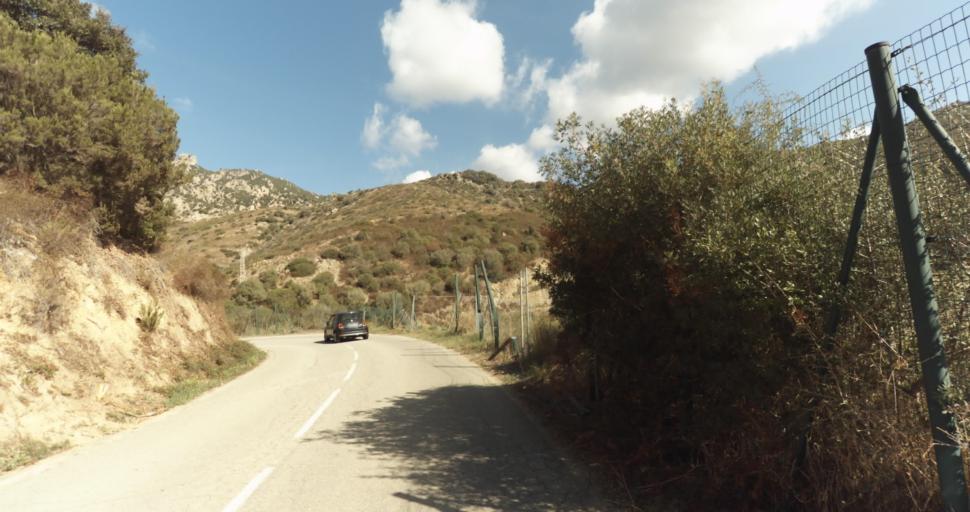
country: FR
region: Corsica
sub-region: Departement de la Corse-du-Sud
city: Ajaccio
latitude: 41.9319
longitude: 8.6919
